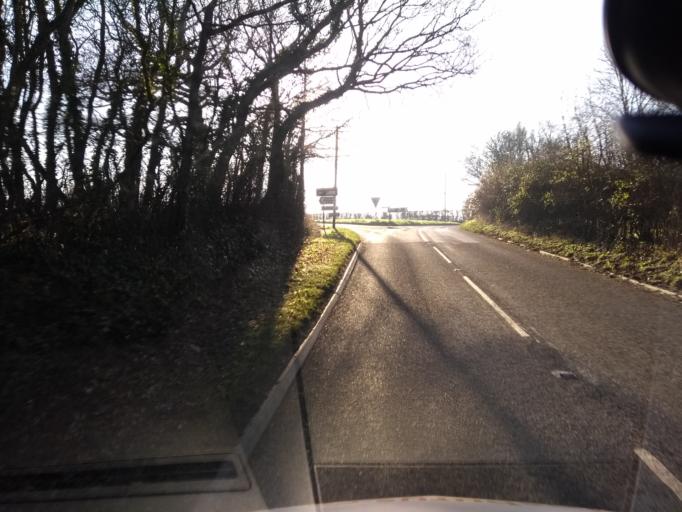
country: GB
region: England
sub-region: Somerset
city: Redlynch
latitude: 51.0869
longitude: -2.4134
